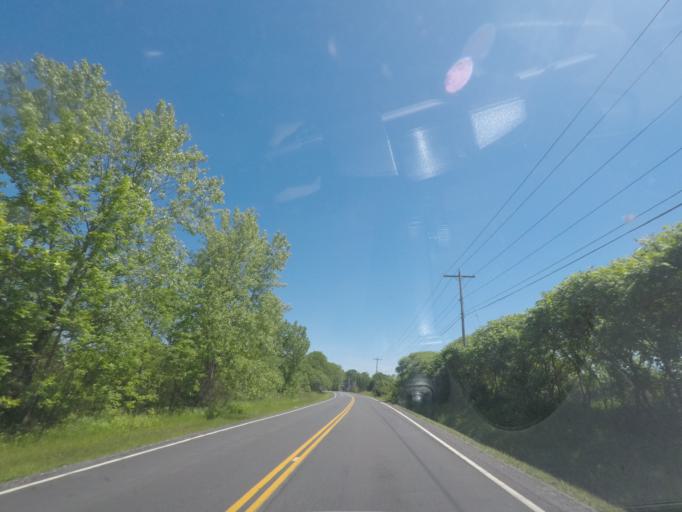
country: US
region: New York
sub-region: Saratoga County
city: Country Knolls
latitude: 42.9006
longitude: -73.8455
